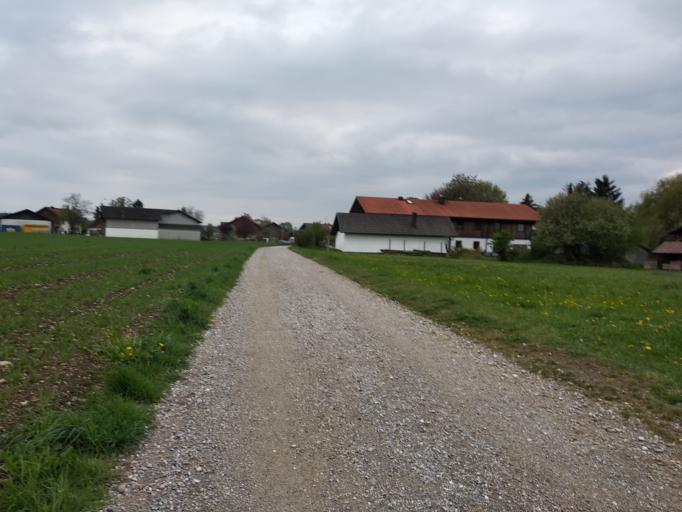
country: DE
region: Bavaria
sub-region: Upper Bavaria
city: Kirchseeon
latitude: 48.0780
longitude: 11.8701
